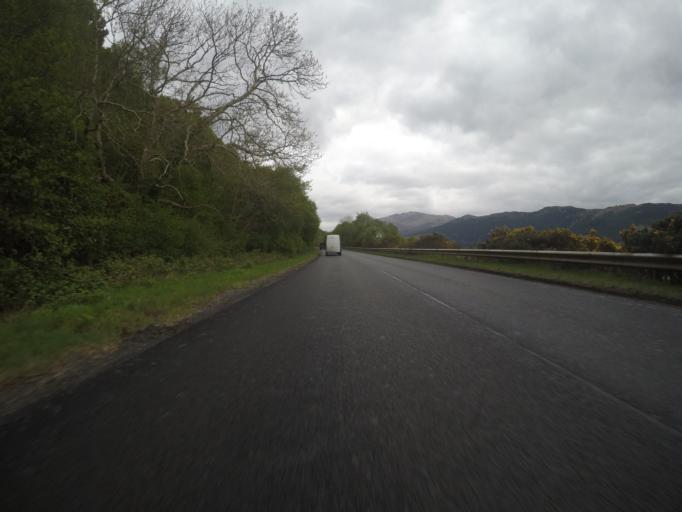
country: GB
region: Scotland
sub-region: Highland
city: Fort William
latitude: 57.2520
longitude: -5.4745
